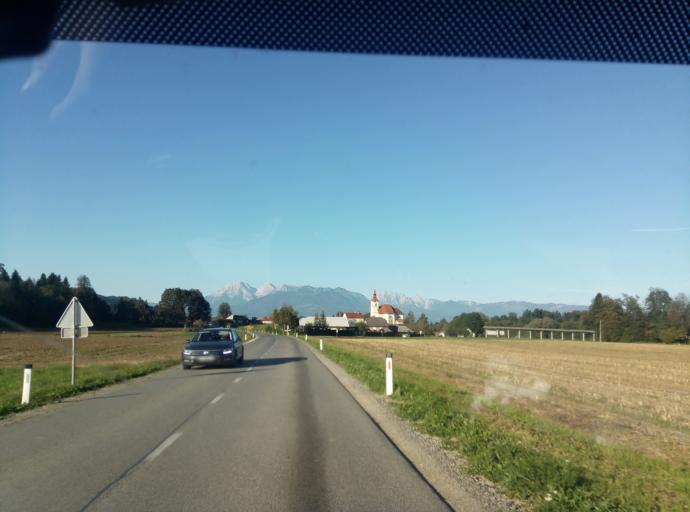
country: SI
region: Vodice
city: Vodice
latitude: 46.1455
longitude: 14.4801
